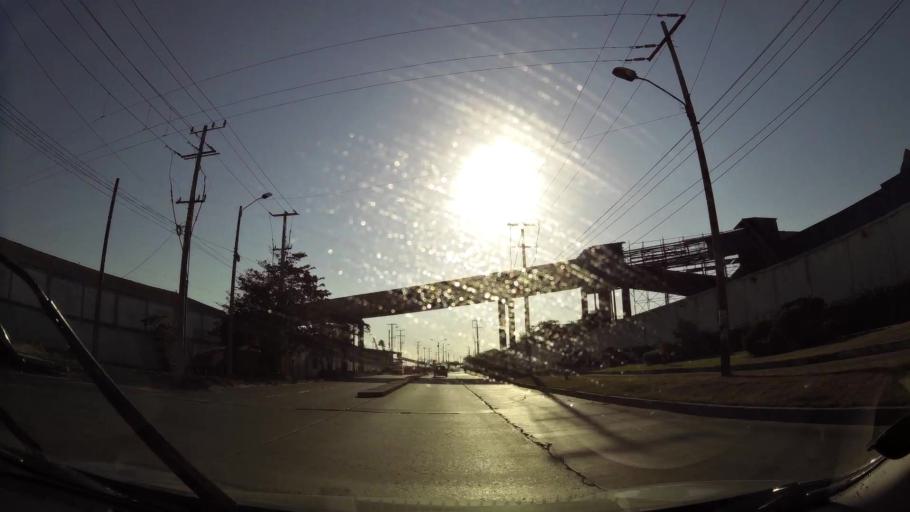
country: CO
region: Atlantico
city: Barranquilla
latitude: 11.0381
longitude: -74.8198
